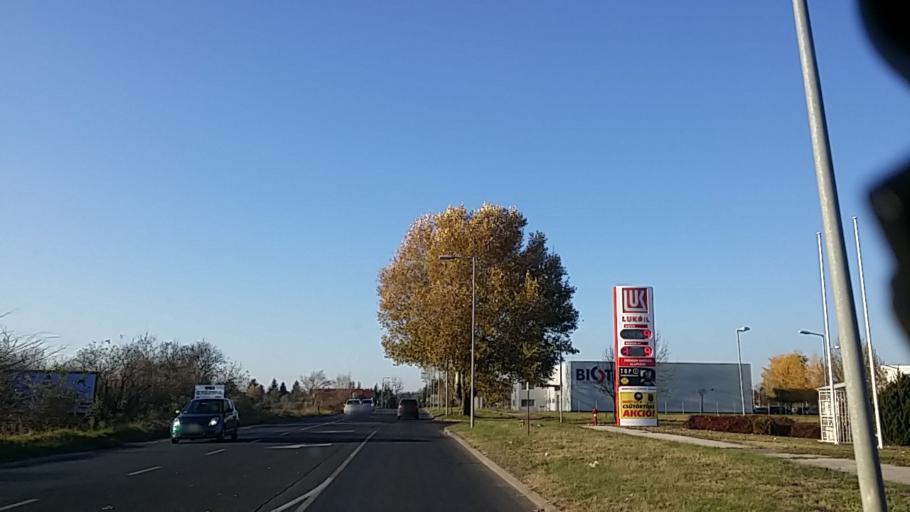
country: HU
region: Budapest
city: Budapest XVII. keruelet
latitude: 47.5011
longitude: 19.2163
